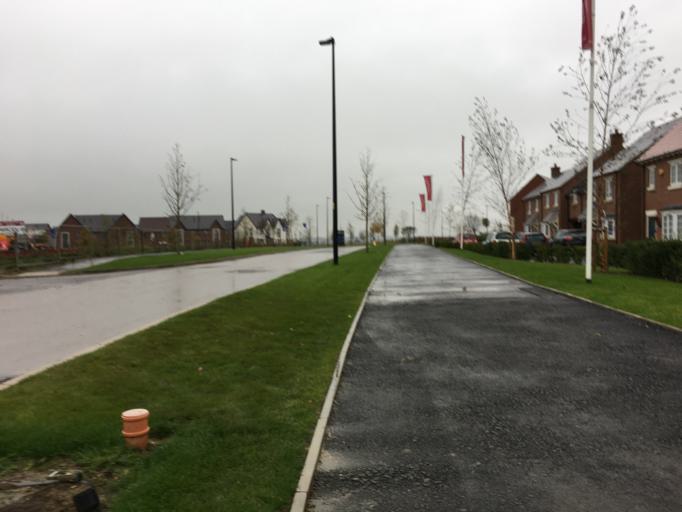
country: GB
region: England
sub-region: Warwickshire
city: Rugby
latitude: 52.3583
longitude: -1.1841
